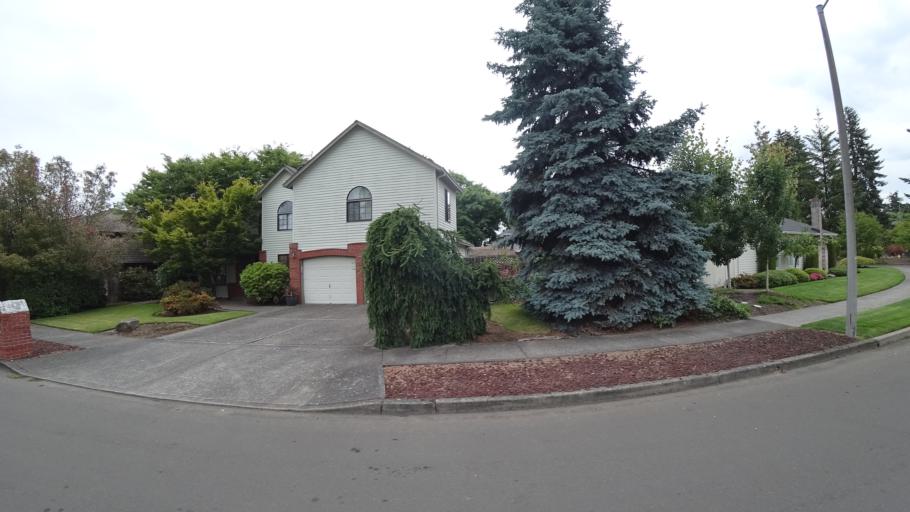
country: US
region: Oregon
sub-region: Multnomah County
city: Fairview
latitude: 45.5384
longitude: -122.4912
